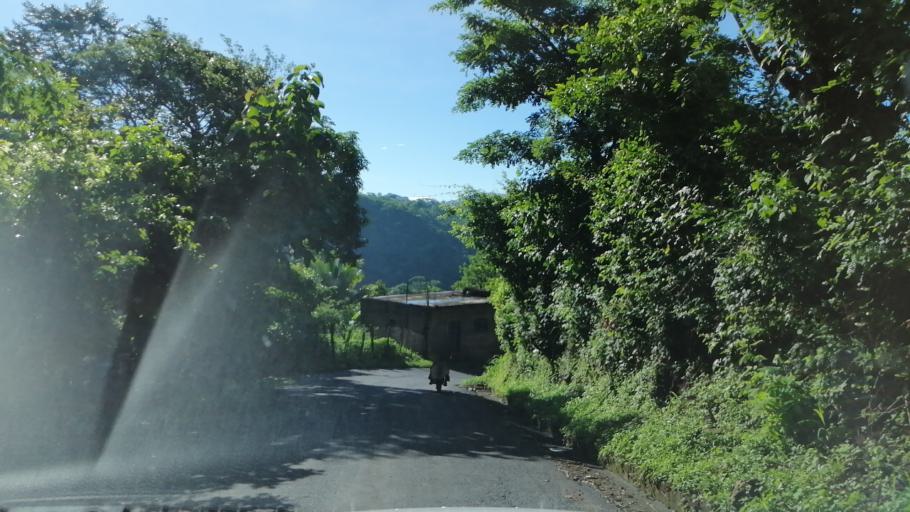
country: SV
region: Morazan
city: Cacaopera
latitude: 13.7711
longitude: -88.0742
